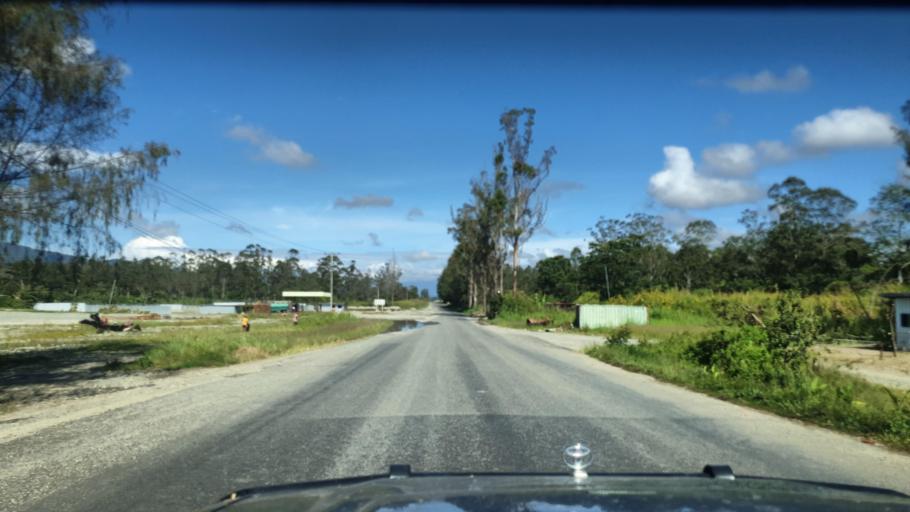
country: PG
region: Western Highlands
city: Rauna
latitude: -5.8345
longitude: 144.3422
